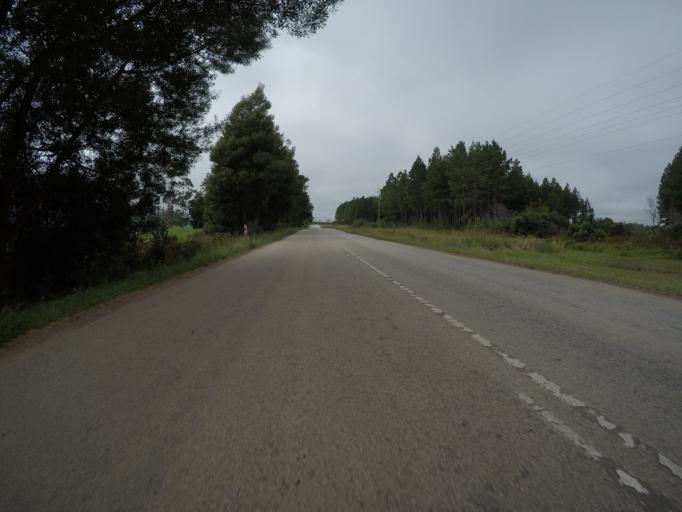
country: ZA
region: Eastern Cape
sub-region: Cacadu District Municipality
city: Kareedouw
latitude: -33.9959
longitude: 24.1328
